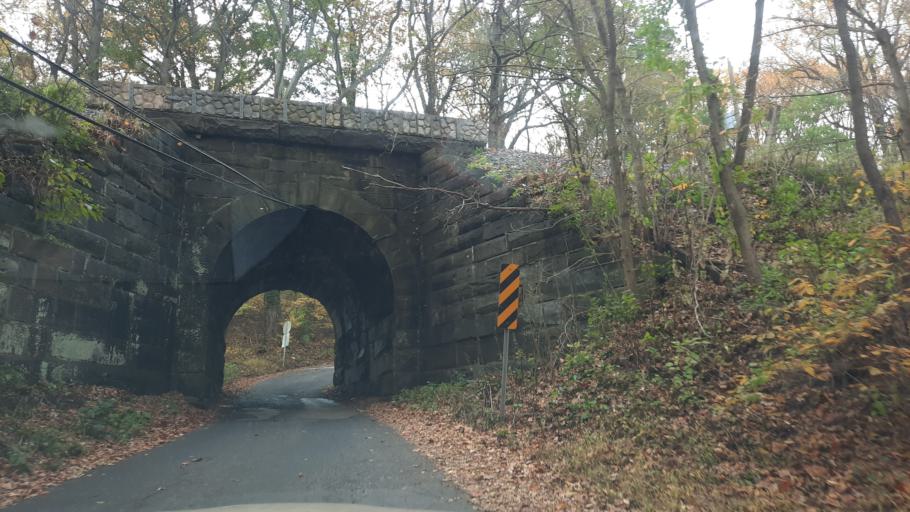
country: US
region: Maryland
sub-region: Montgomery County
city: Gaithersburg
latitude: 39.1547
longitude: -77.2379
